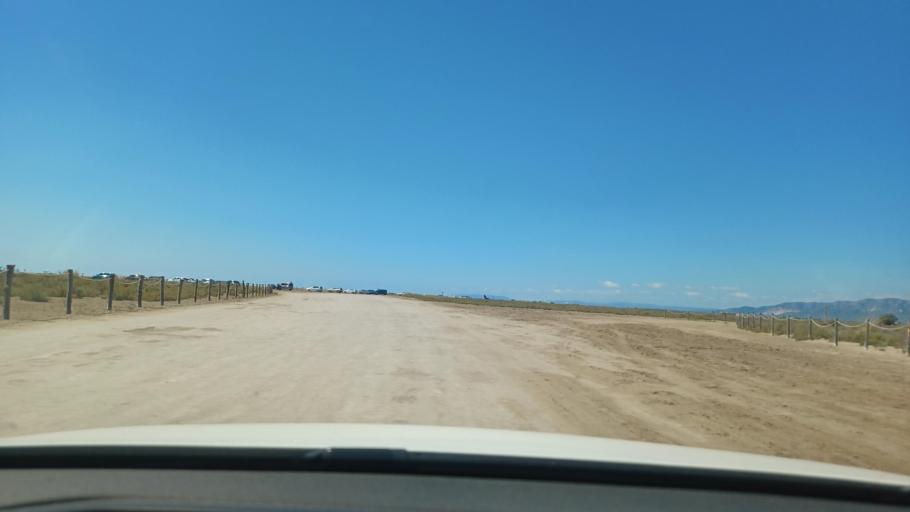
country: ES
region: Catalonia
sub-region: Provincia de Tarragona
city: Deltebre
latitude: 40.6540
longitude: 0.7818
